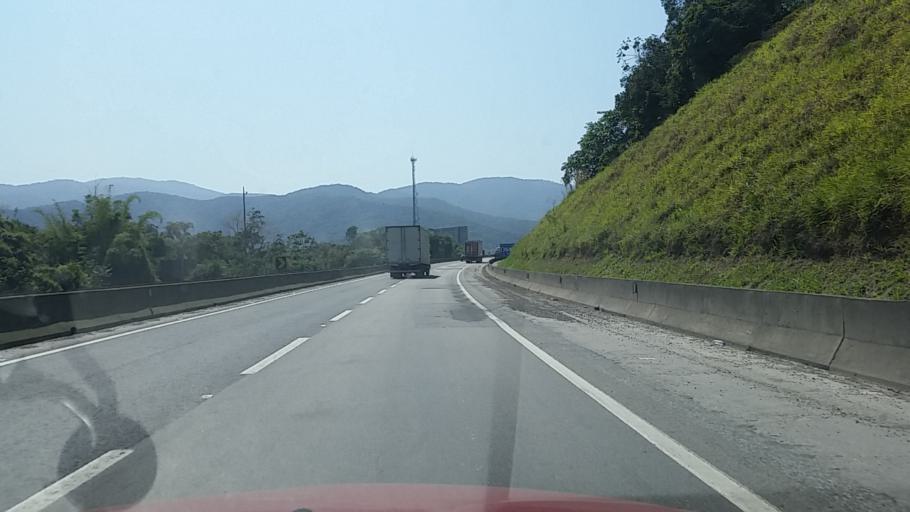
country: BR
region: Sao Paulo
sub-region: Miracatu
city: Miracatu
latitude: -24.1554
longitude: -47.3247
